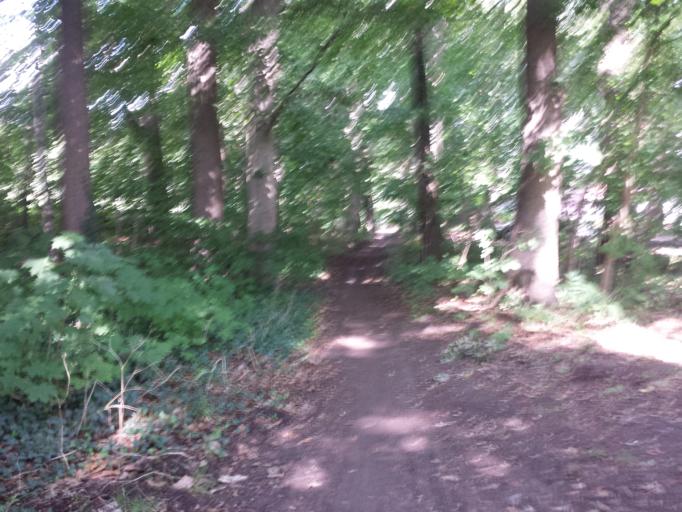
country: DE
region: North Rhine-Westphalia
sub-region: Regierungsbezirk Detmold
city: Guetersloh
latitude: 51.8958
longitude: 8.3955
